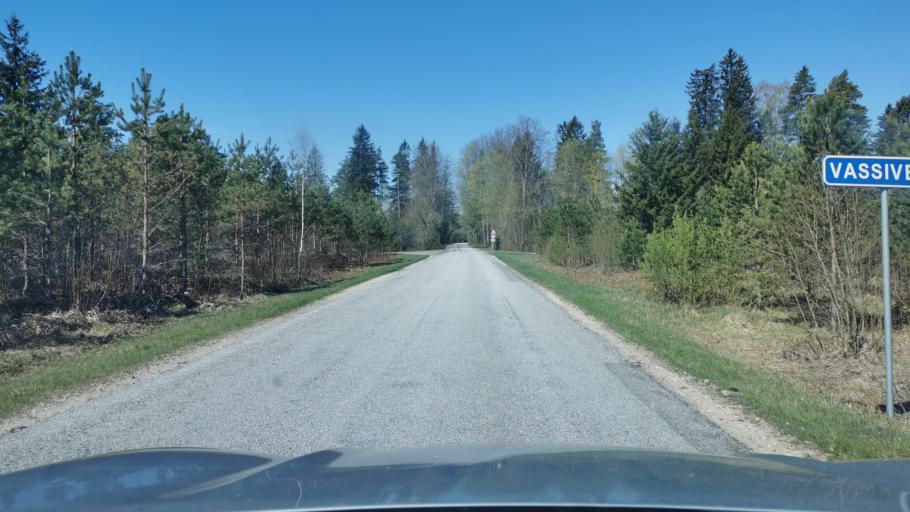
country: EE
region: Laeaene-Virumaa
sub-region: Vinni vald
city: Vinni
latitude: 59.0459
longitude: 26.6234
